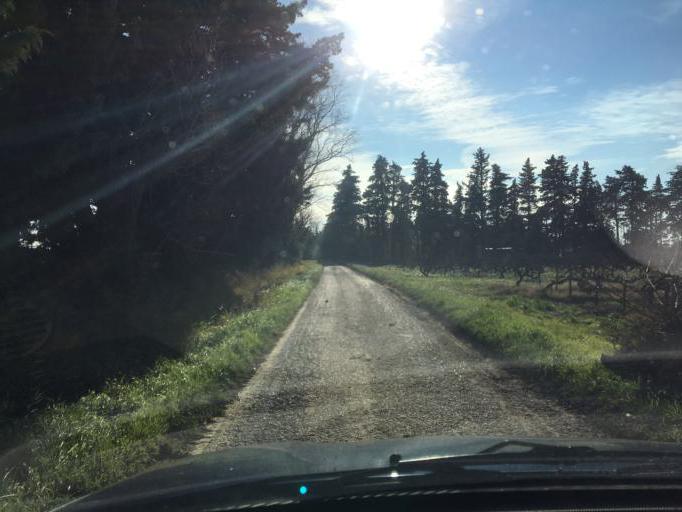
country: FR
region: Provence-Alpes-Cote d'Azur
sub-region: Departement du Vaucluse
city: Camaret-sur-Aigues
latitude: 44.1575
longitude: 4.8904
